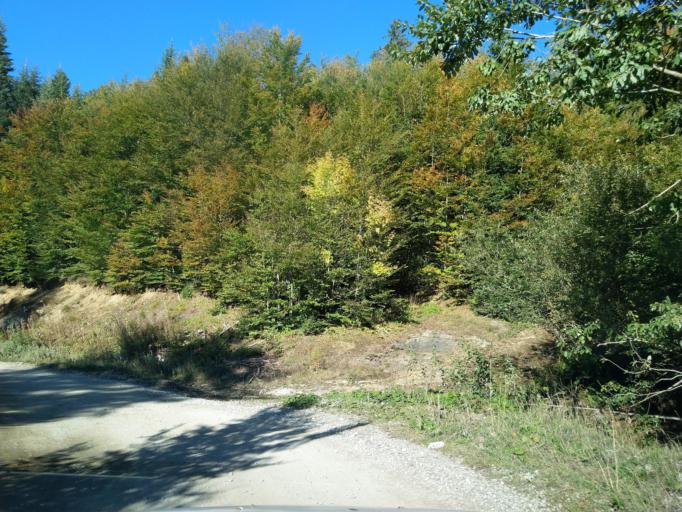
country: RS
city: Sokolovica
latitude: 43.3663
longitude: 20.2595
